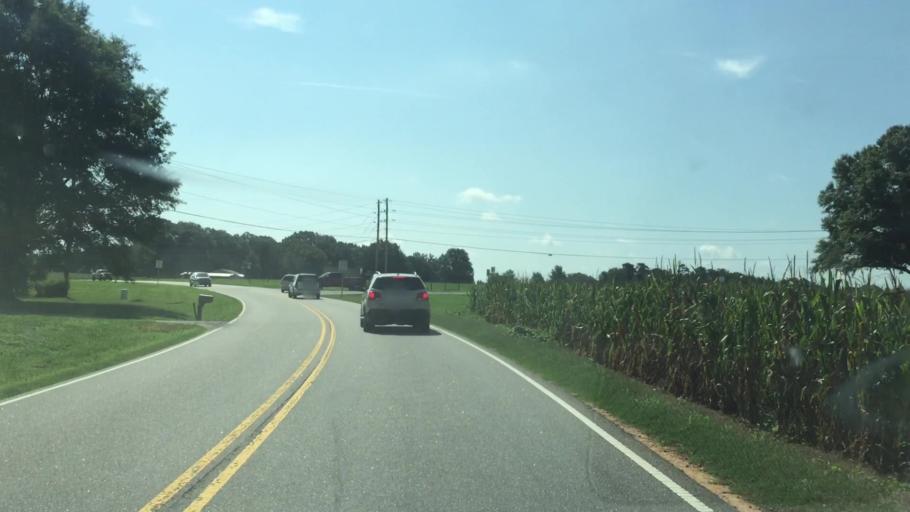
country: US
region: North Carolina
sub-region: Union County
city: Unionville
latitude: 35.1207
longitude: -80.4251
